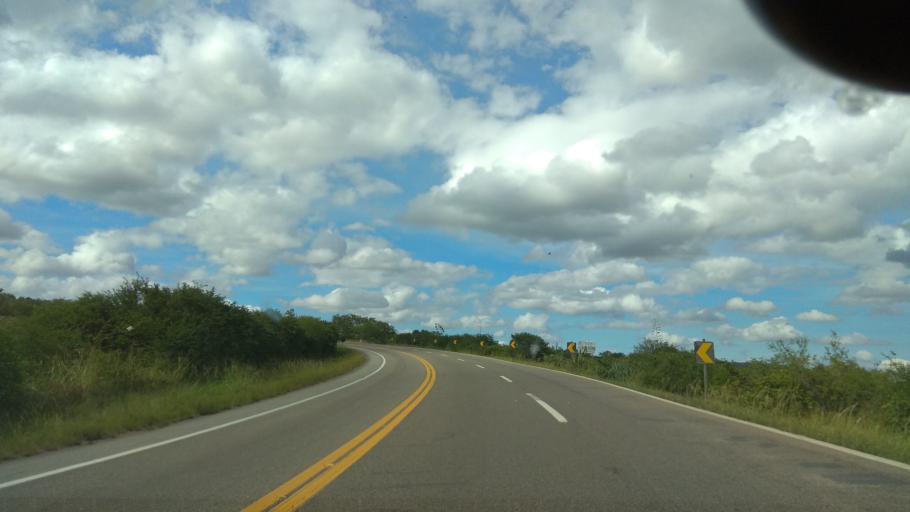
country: BR
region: Bahia
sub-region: Amargosa
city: Amargosa
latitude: -12.9346
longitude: -39.8915
